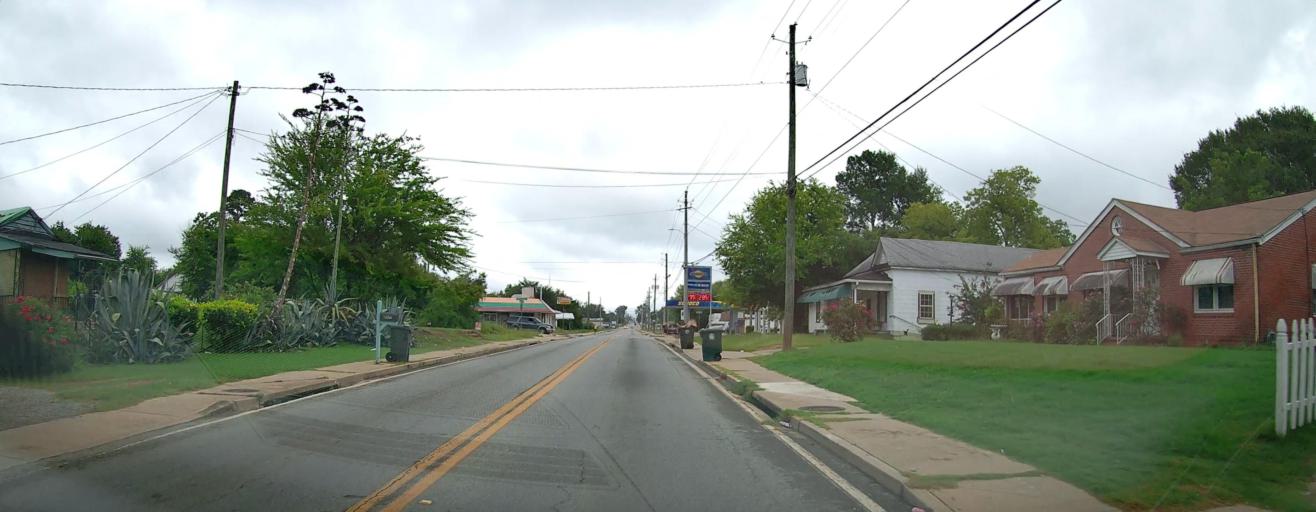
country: US
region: Georgia
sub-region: Bibb County
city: Macon
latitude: 32.7936
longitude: -83.6548
